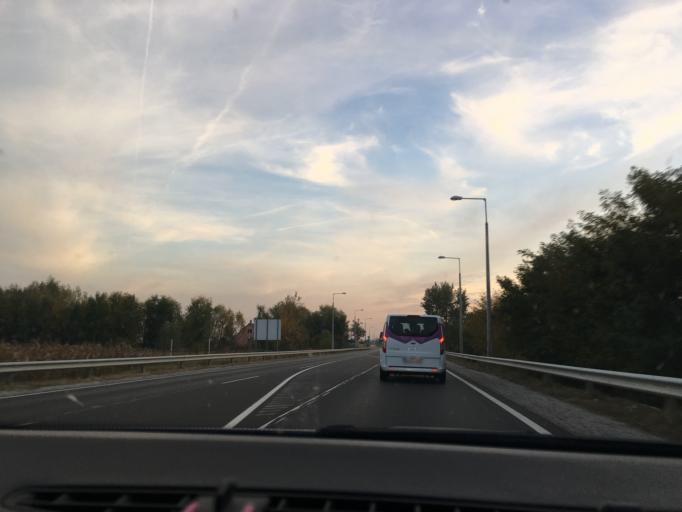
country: HU
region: Hajdu-Bihar
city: Teglas
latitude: 47.7113
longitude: 21.6598
